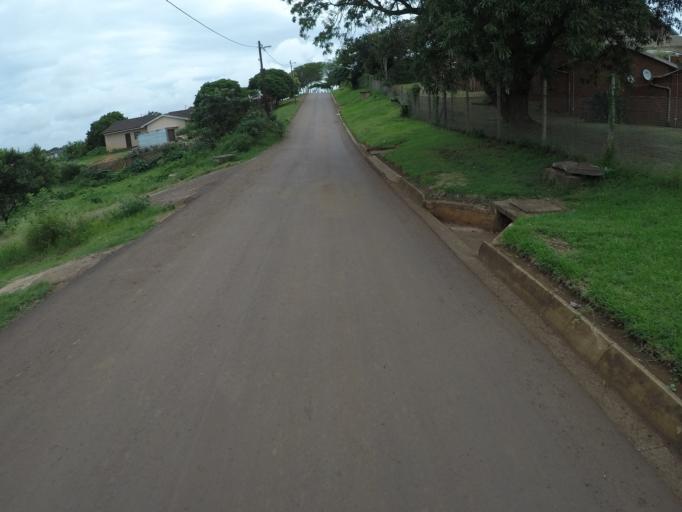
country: ZA
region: KwaZulu-Natal
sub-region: uThungulu District Municipality
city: Empangeni
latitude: -28.7798
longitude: 31.8672
